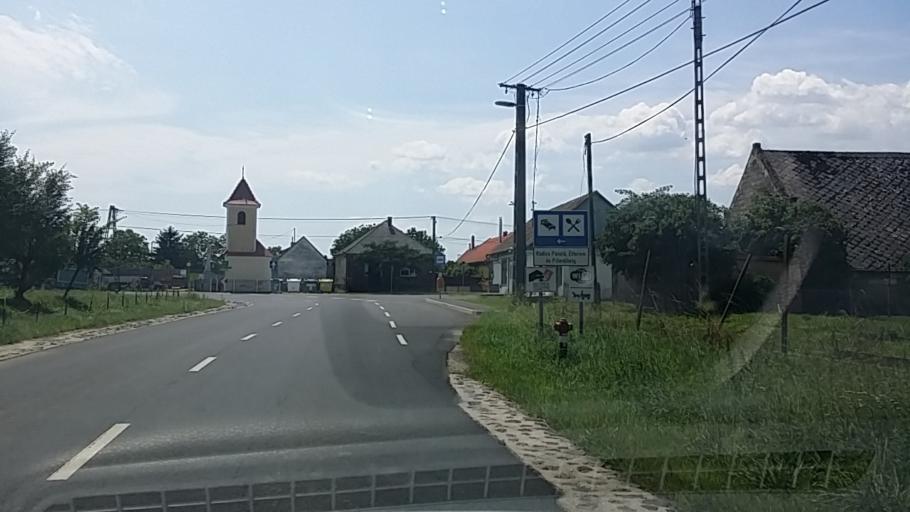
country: HU
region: Zala
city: Letenye
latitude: 46.4214
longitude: 16.7439
